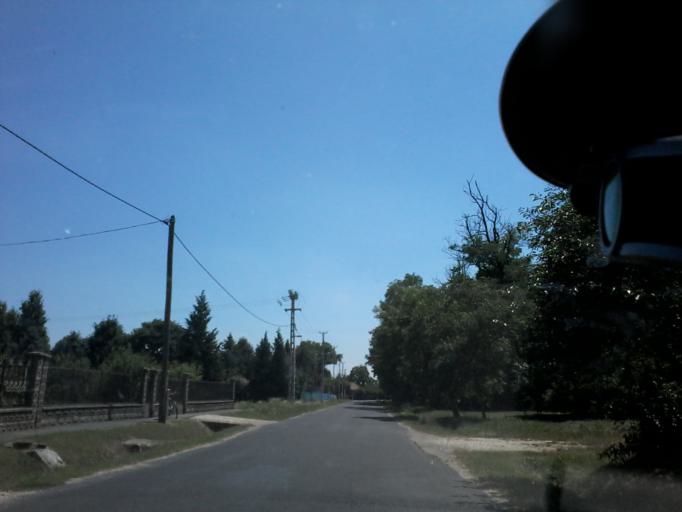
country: HU
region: Vas
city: Celldomolk
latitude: 47.1945
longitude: 17.1090
